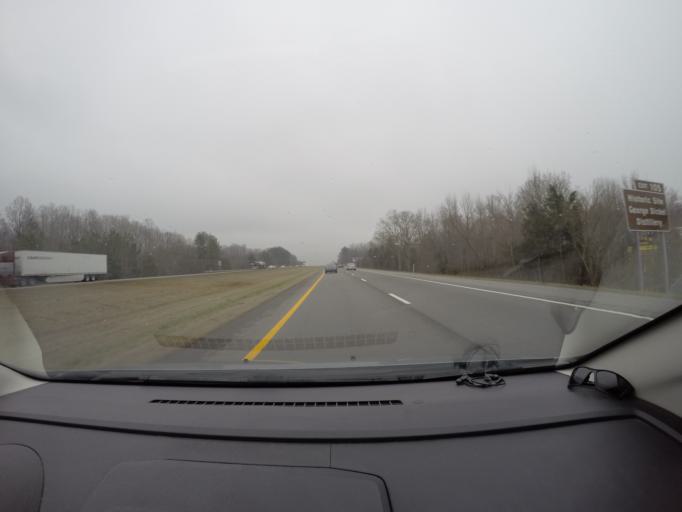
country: US
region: Tennessee
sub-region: Coffee County
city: New Union
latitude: 35.5404
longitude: -86.1761
